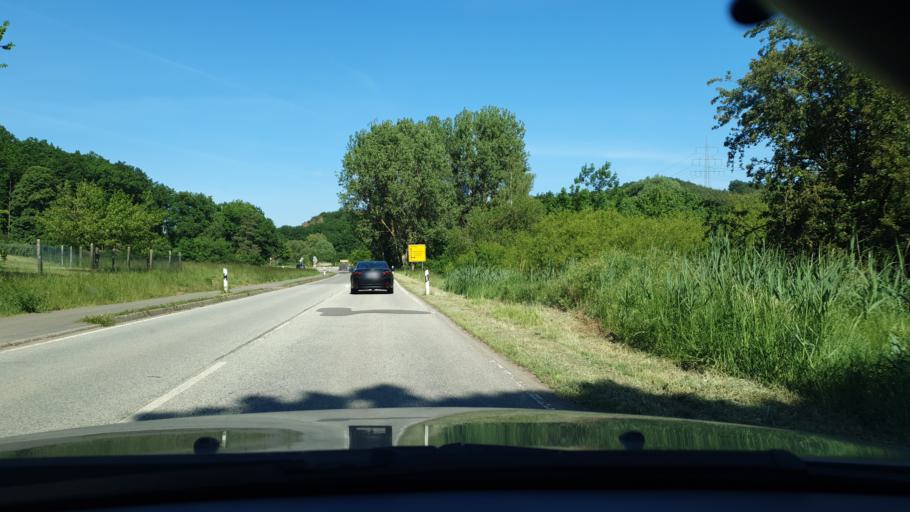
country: DE
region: Rheinland-Pfalz
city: Otterbach
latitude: 49.4901
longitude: 7.7563
